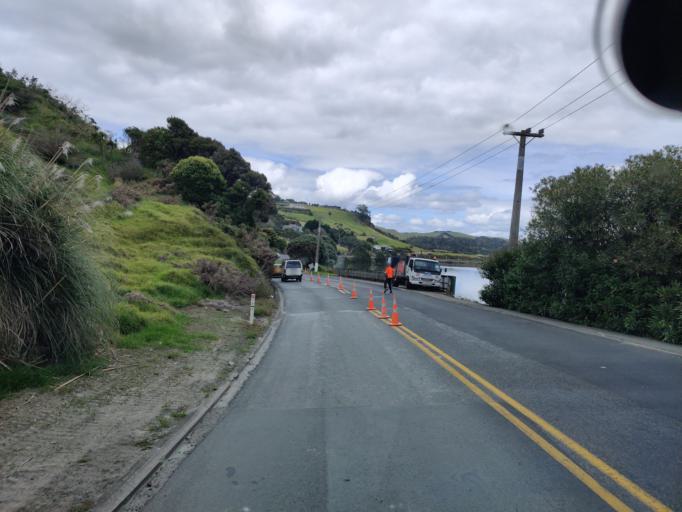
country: NZ
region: Northland
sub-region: Far North District
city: Taipa
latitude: -34.9951
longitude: 173.4726
